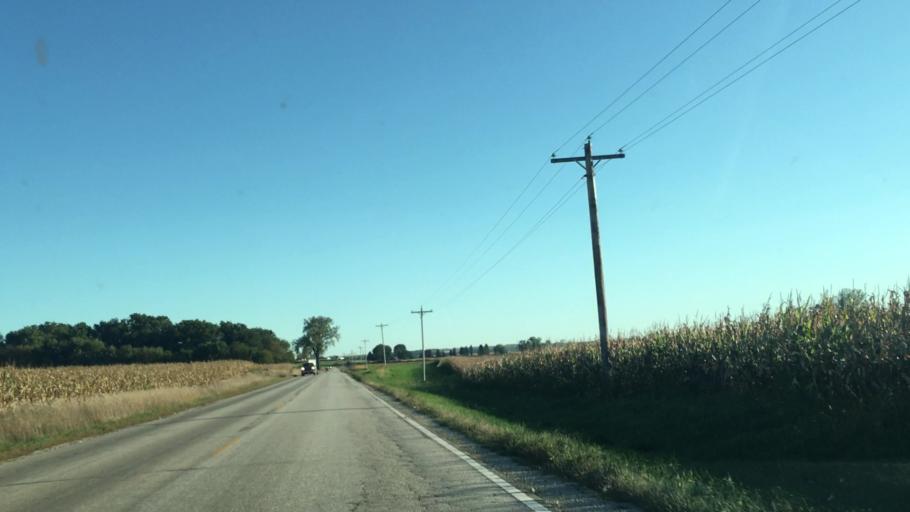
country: US
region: Minnesota
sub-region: Fillmore County
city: Chatfield
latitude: 43.8250
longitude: -92.0694
